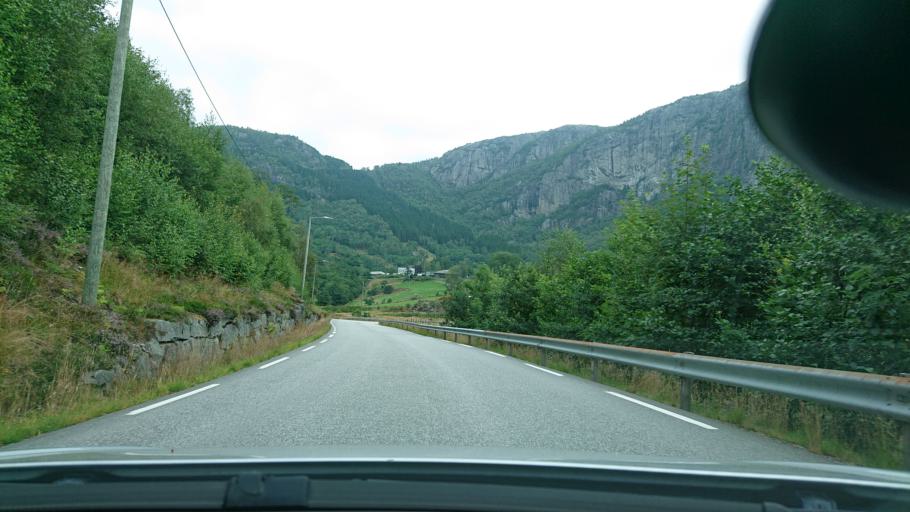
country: NO
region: Rogaland
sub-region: Hjelmeland
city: Hjelmelandsvagen
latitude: 59.2309
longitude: 6.1959
